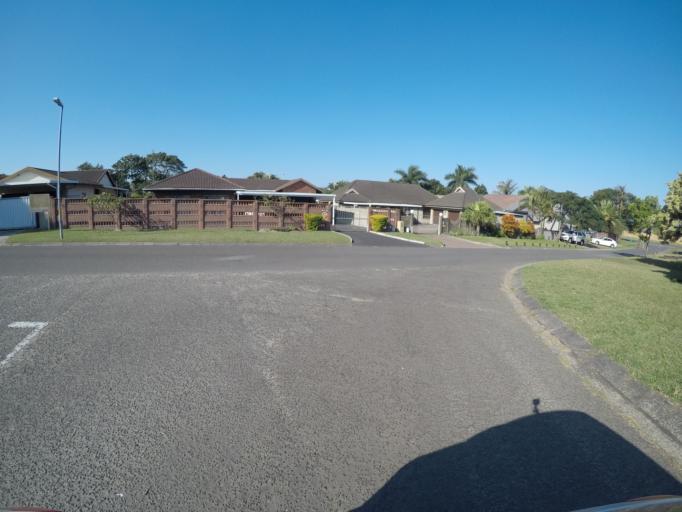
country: ZA
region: KwaZulu-Natal
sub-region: uThungulu District Municipality
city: Richards Bay
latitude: -28.7653
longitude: 32.0587
